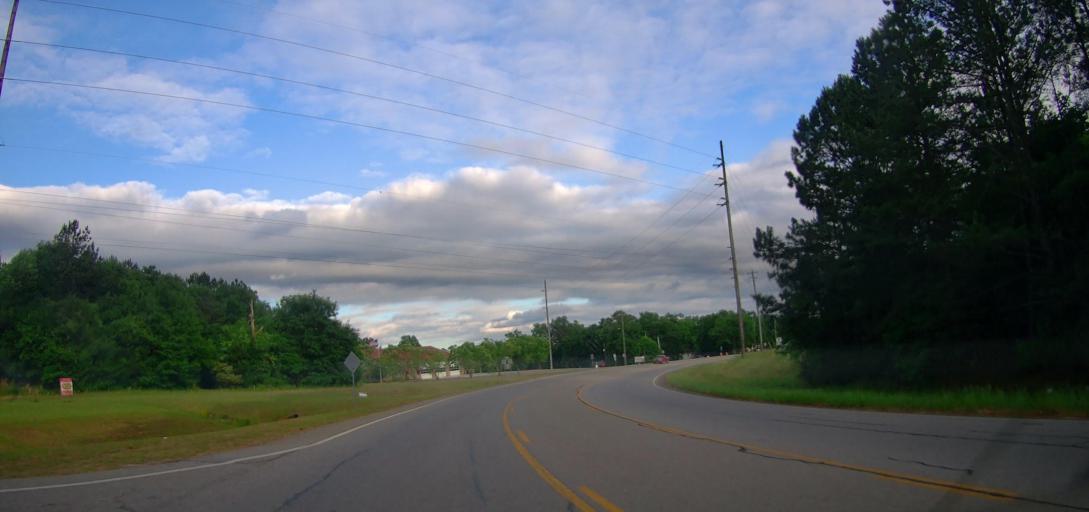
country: US
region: Georgia
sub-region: Oconee County
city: Watkinsville
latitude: 33.8797
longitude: -83.4147
